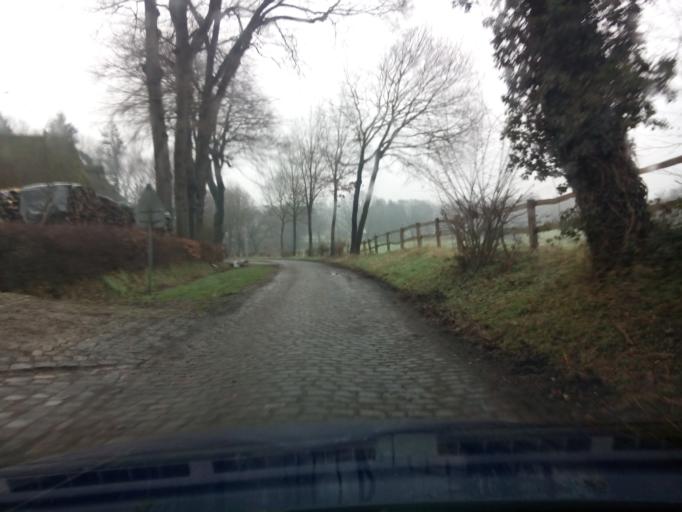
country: DE
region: Lower Saxony
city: Osterholz-Scharmbeck
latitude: 53.2488
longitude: 8.8012
